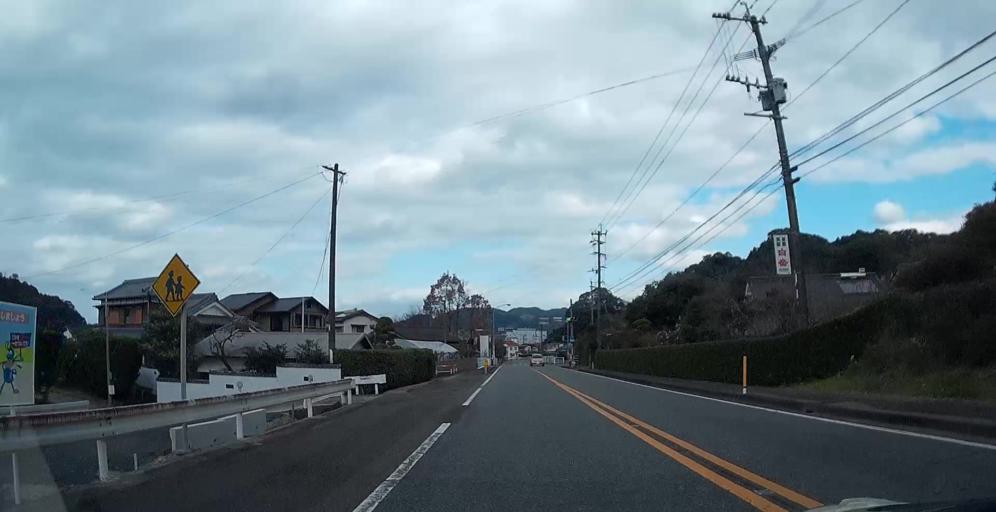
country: JP
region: Kumamoto
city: Minamata
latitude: 32.3458
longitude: 130.5028
